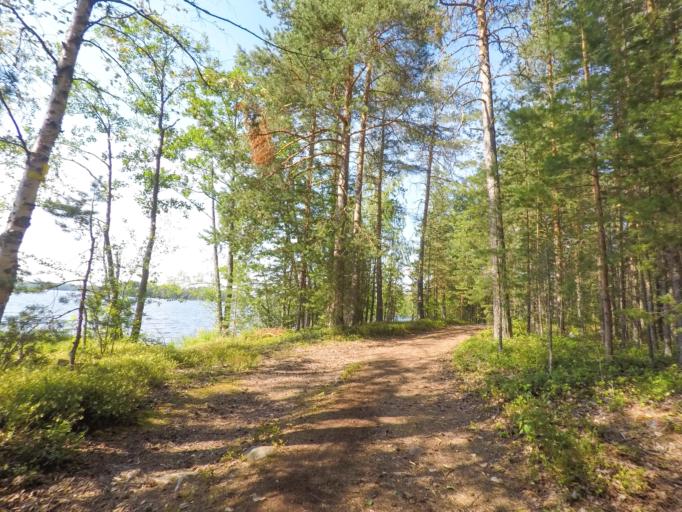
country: FI
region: Southern Savonia
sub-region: Mikkeli
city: Puumala
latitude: 61.4921
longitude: 28.1669
